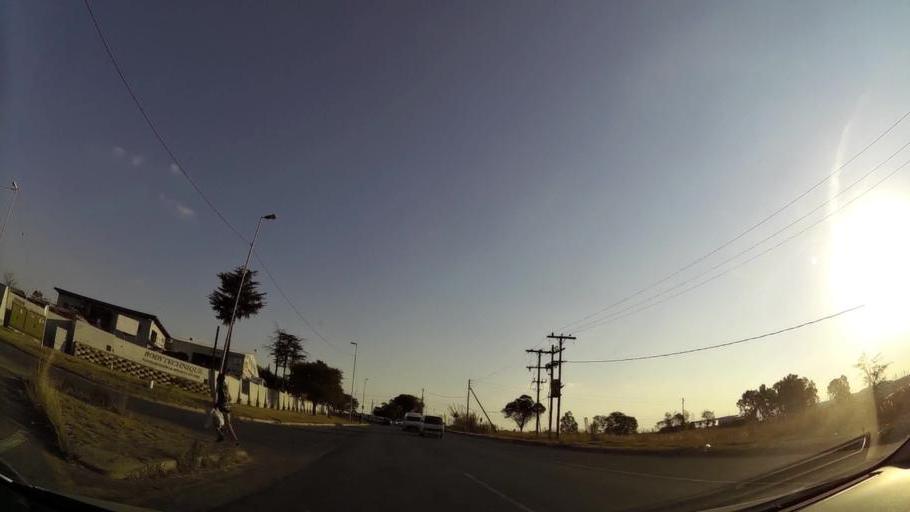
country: ZA
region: Gauteng
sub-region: City of Johannesburg Metropolitan Municipality
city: Midrand
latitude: -26.0316
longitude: 28.1393
